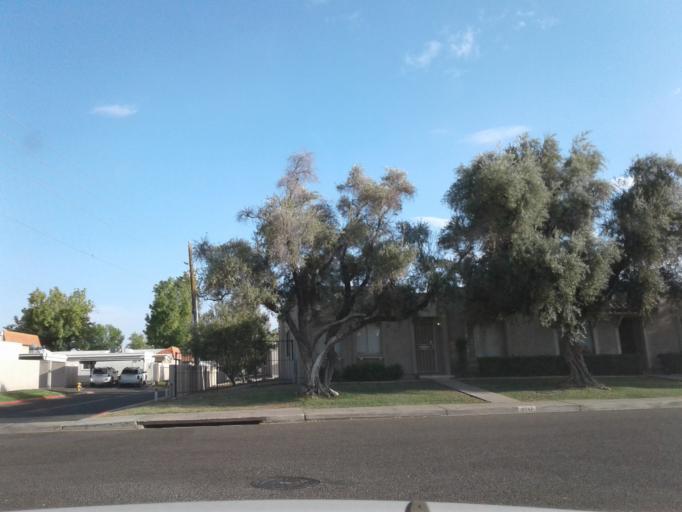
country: US
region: Arizona
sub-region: Maricopa County
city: Scottsdale
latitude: 33.5131
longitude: -111.9046
